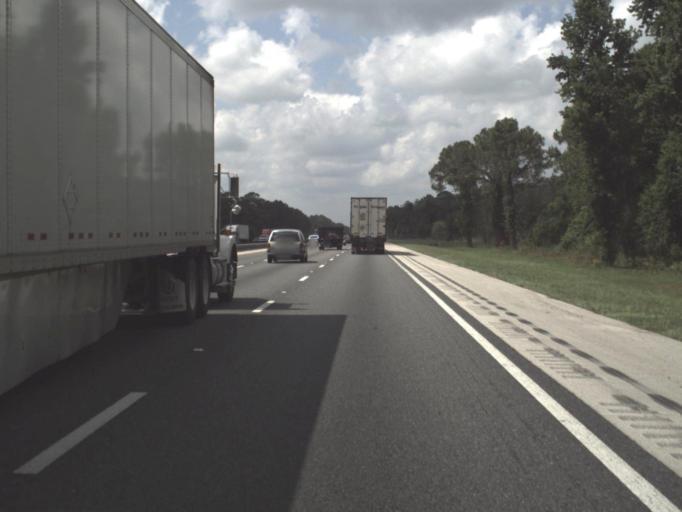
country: US
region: Florida
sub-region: Saint Johns County
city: Saint Augustine South
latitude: 29.8652
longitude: -81.3960
